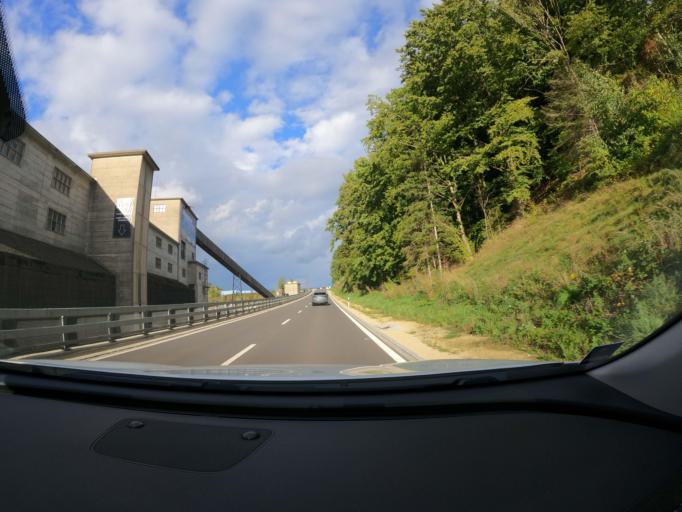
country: CH
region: Aargau
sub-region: Bezirk Brugg
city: Brugg
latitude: 47.4720
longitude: 8.1994
